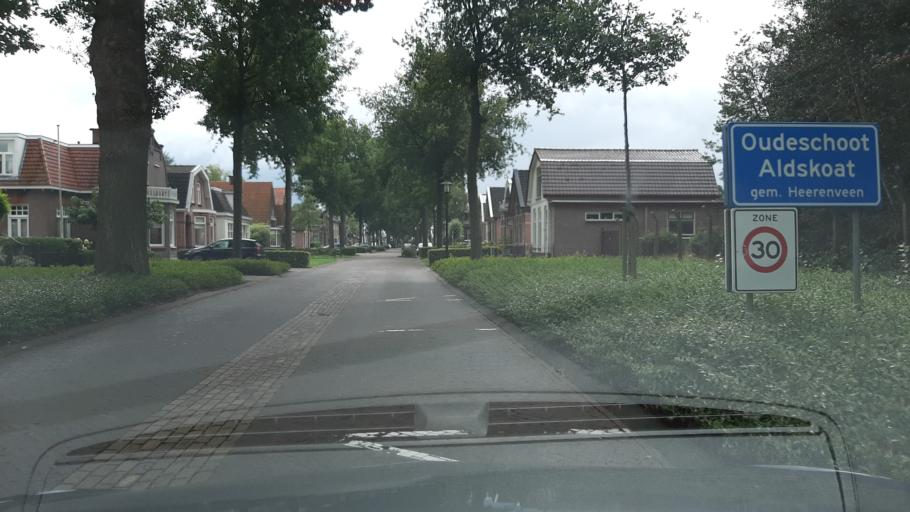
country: NL
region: Friesland
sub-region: Gemeente Heerenveen
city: Oudeschoot
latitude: 52.9369
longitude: 5.9512
